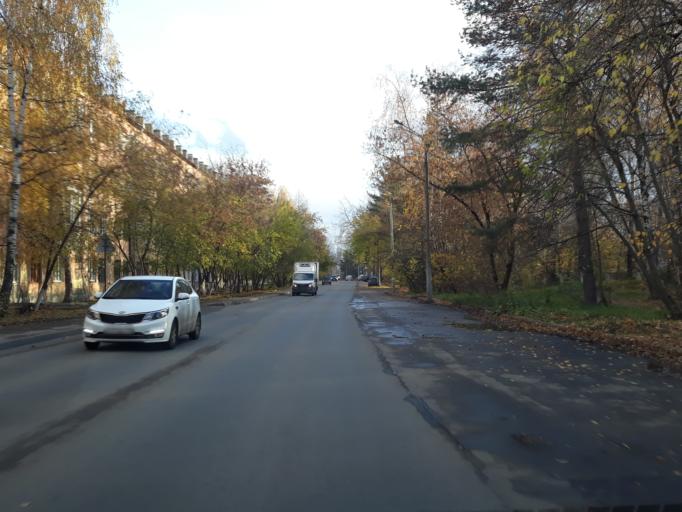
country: RU
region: Nizjnij Novgorod
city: Neklyudovo
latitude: 56.3417
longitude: 43.8660
